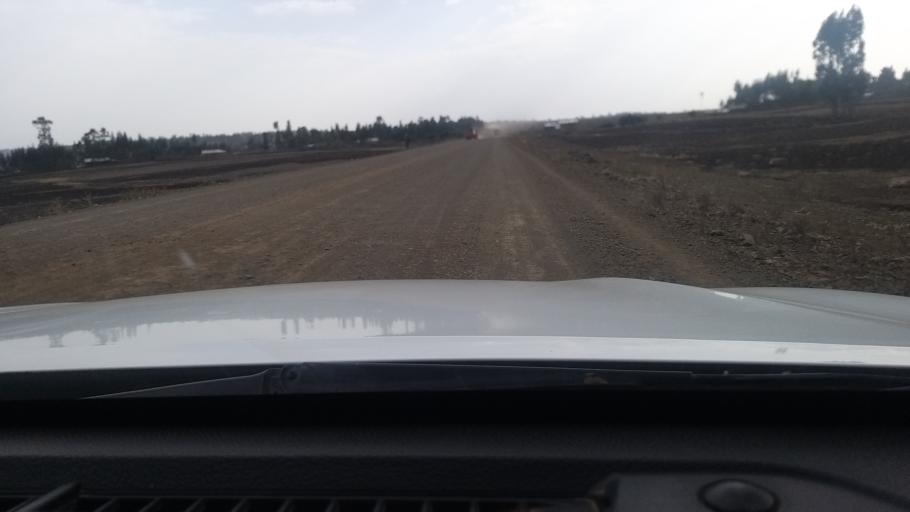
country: ET
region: Amhara
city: Were Ilu
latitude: 10.4516
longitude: 39.2075
